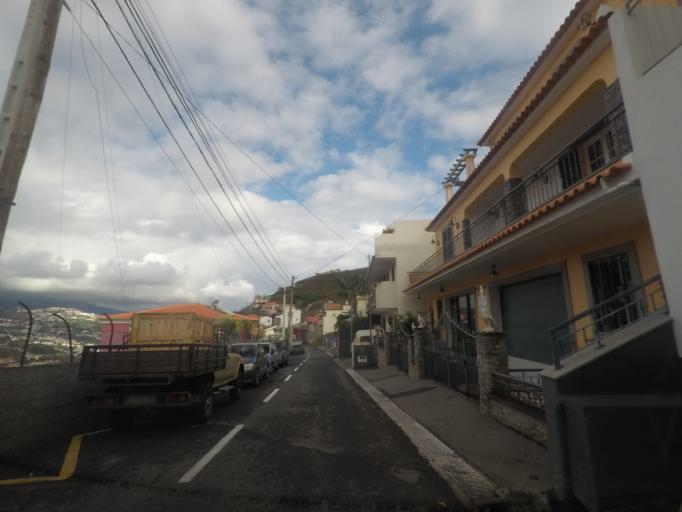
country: PT
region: Madeira
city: Camara de Lobos
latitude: 32.6561
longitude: -16.9957
